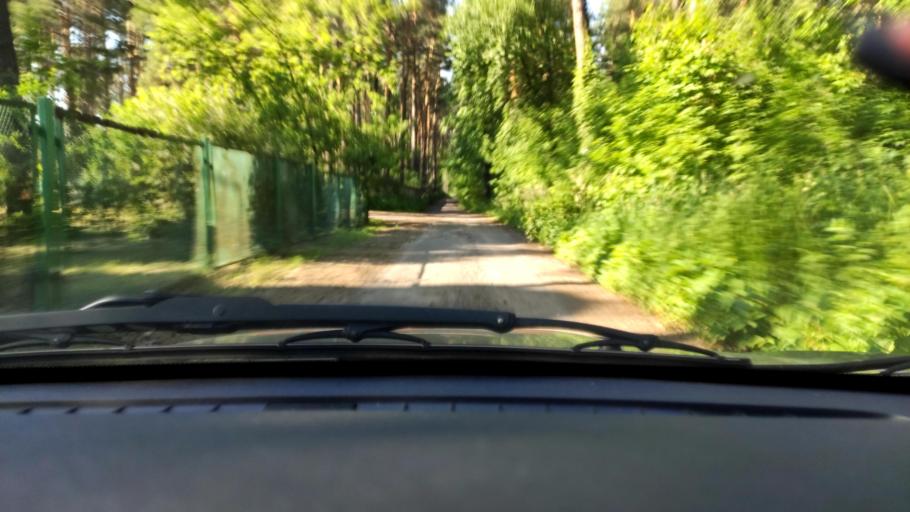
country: RU
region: Voronezj
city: Somovo
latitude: 51.7585
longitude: 39.3747
